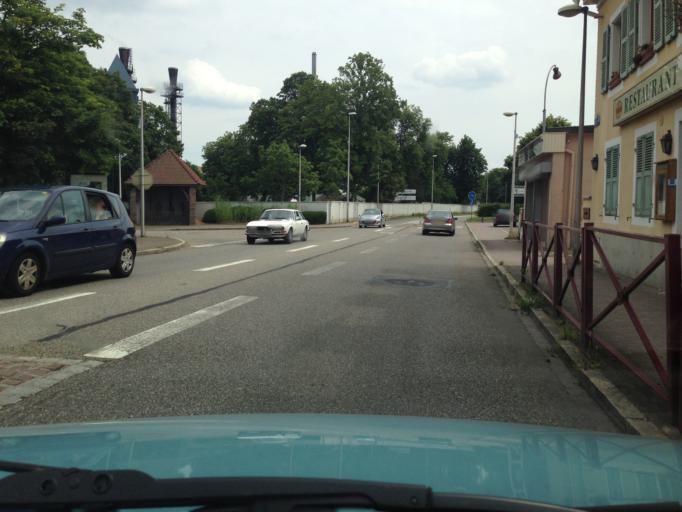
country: FR
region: Alsace
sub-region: Departement du Haut-Rhin
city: Vieux-Thann
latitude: 47.8083
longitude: 7.1080
